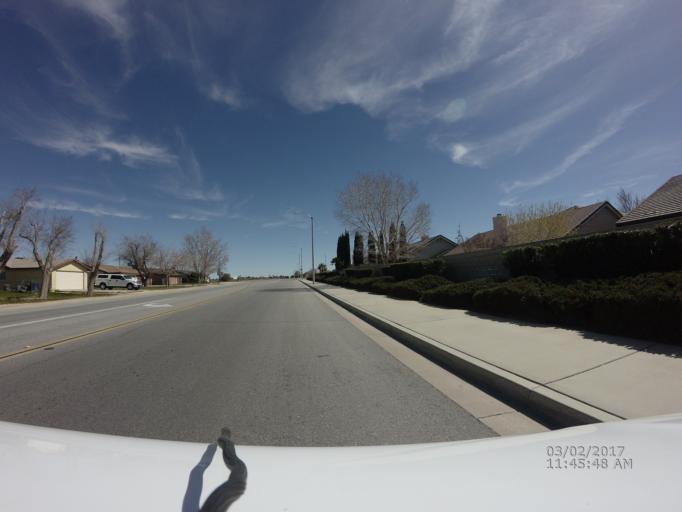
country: US
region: California
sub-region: Los Angeles County
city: Quartz Hill
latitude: 34.6528
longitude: -118.2027
